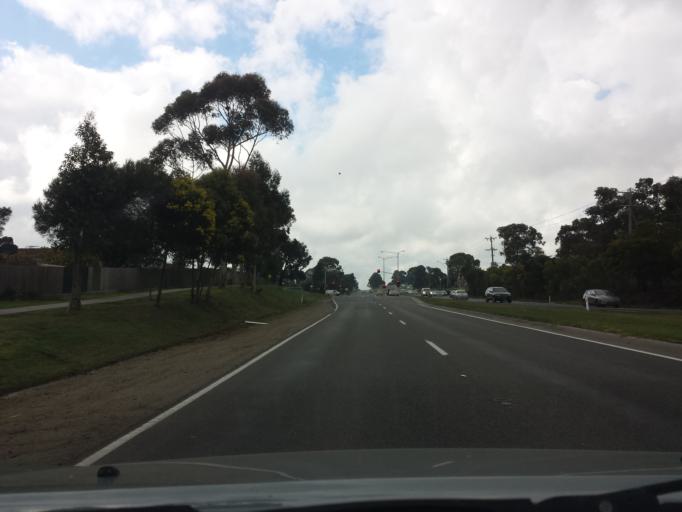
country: AU
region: Victoria
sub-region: Casey
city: Endeavour Hills
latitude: -37.9746
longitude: 145.2561
